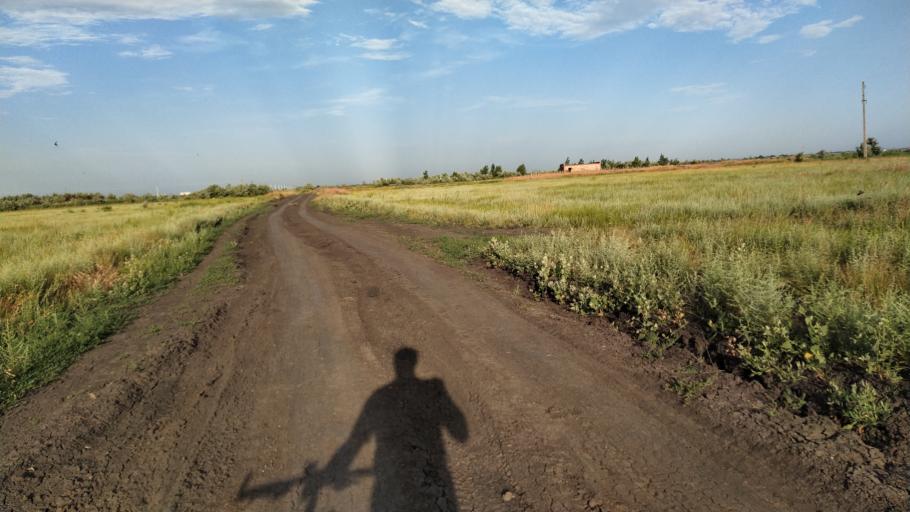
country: RU
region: Rostov
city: Kuleshovka
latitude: 47.1385
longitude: 39.6393
